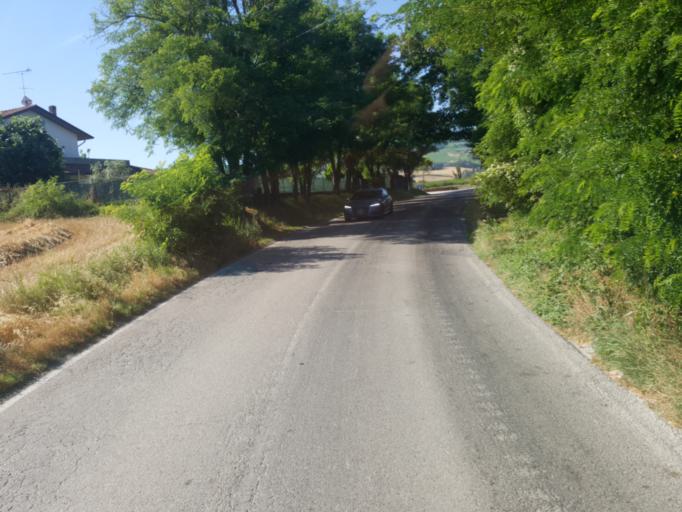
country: IT
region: The Marches
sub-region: Provincia di Pesaro e Urbino
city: Padiglione
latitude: 43.8465
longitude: 12.7206
